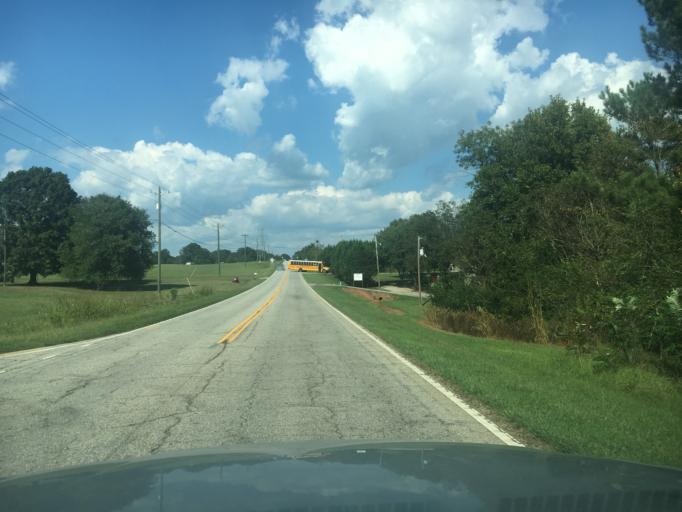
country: US
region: South Carolina
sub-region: Pickens County
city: Liberty
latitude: 34.7381
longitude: -82.6665
